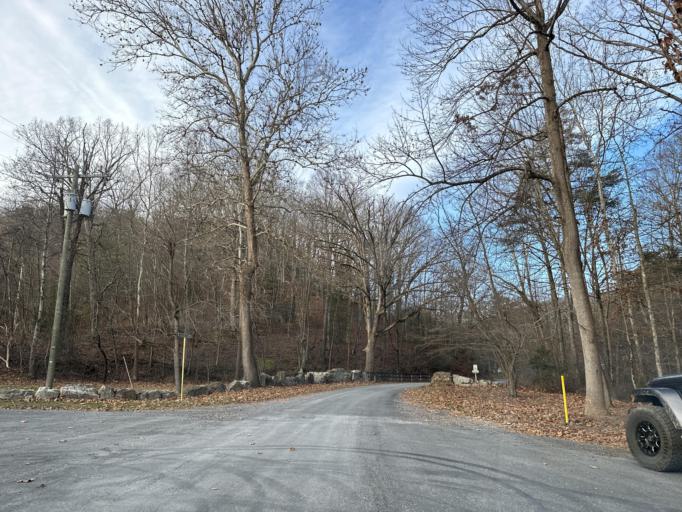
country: US
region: Virginia
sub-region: City of Staunton
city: Staunton
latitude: 38.2123
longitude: -79.2267
